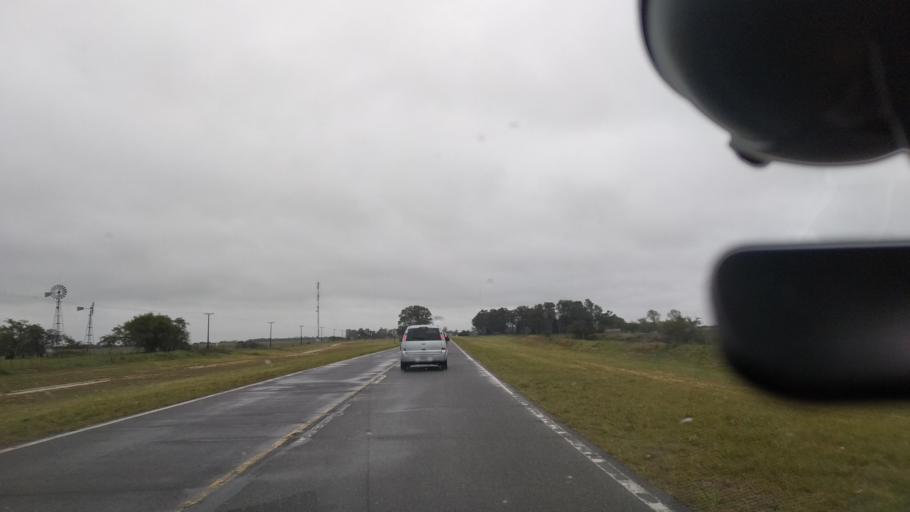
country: AR
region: Buenos Aires
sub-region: Partido de Castelli
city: Castelli
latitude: -35.9892
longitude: -57.4499
